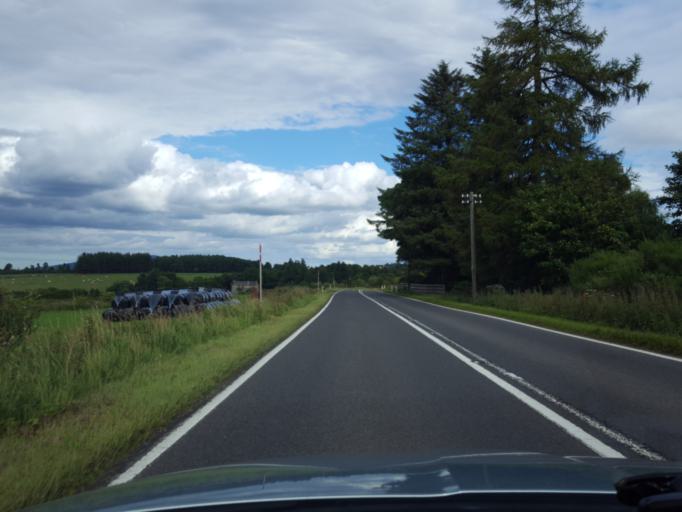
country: GB
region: Scotland
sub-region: Moray
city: Rothes
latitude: 57.4460
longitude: -3.2698
